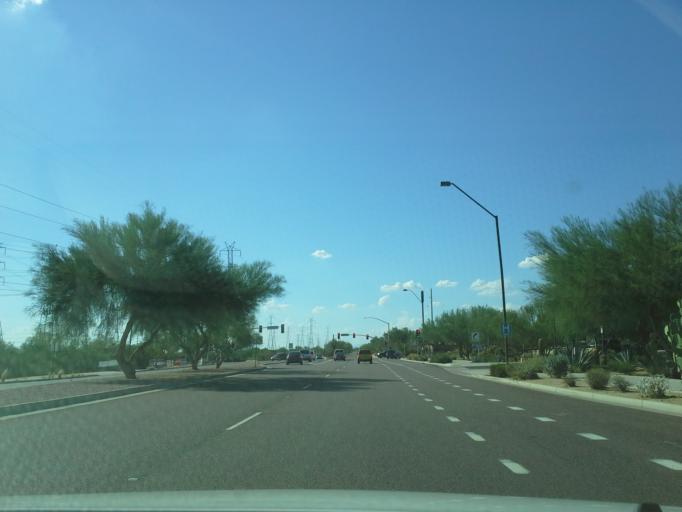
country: US
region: Arizona
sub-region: Maricopa County
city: Paradise Valley
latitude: 33.6706
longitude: -111.9064
